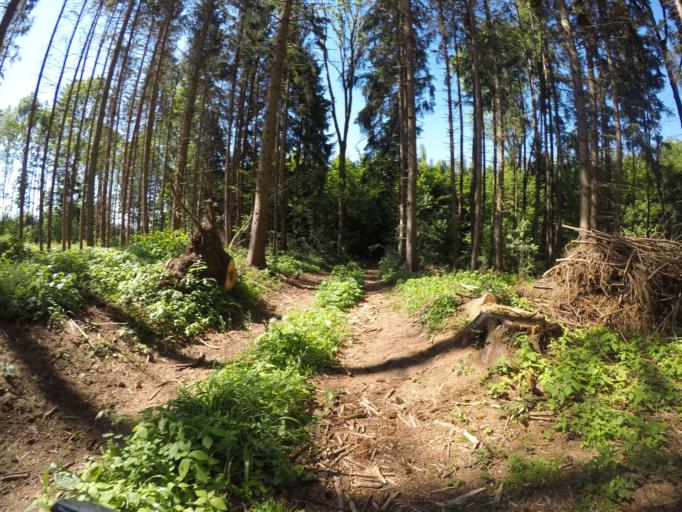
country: DE
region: Bavaria
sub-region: Lower Bavaria
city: Kumhausen
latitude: 48.5143
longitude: 12.1809
